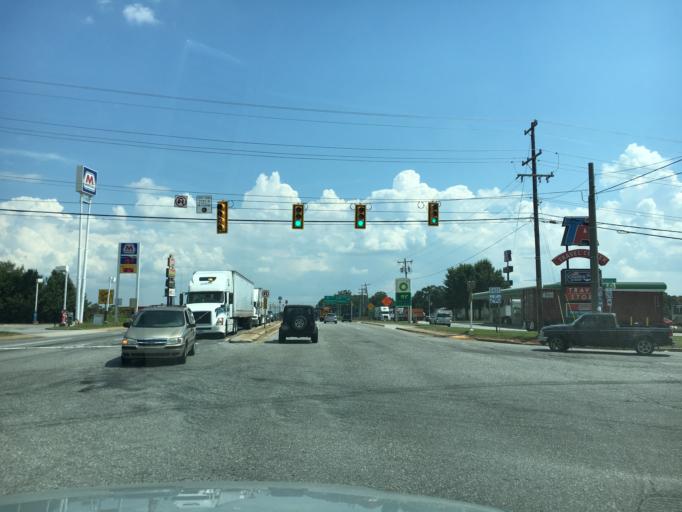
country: US
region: South Carolina
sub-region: Spartanburg County
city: Wellford
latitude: 34.9162
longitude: -82.1102
